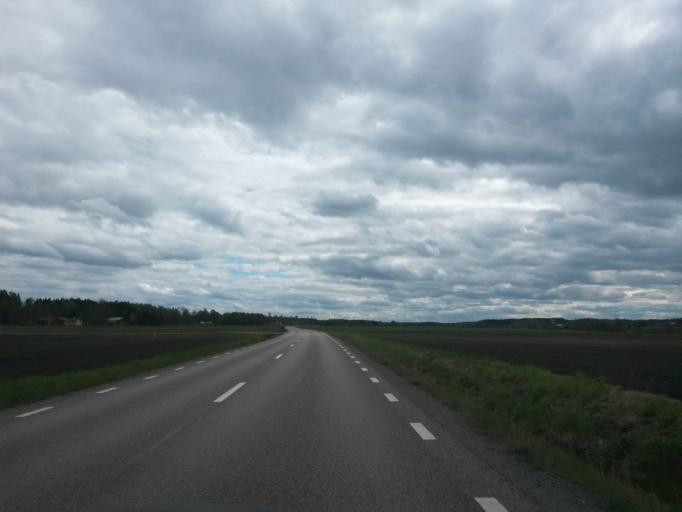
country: SE
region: Vaestra Goetaland
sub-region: Grastorps Kommun
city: Graestorp
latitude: 58.2856
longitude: 12.6718
